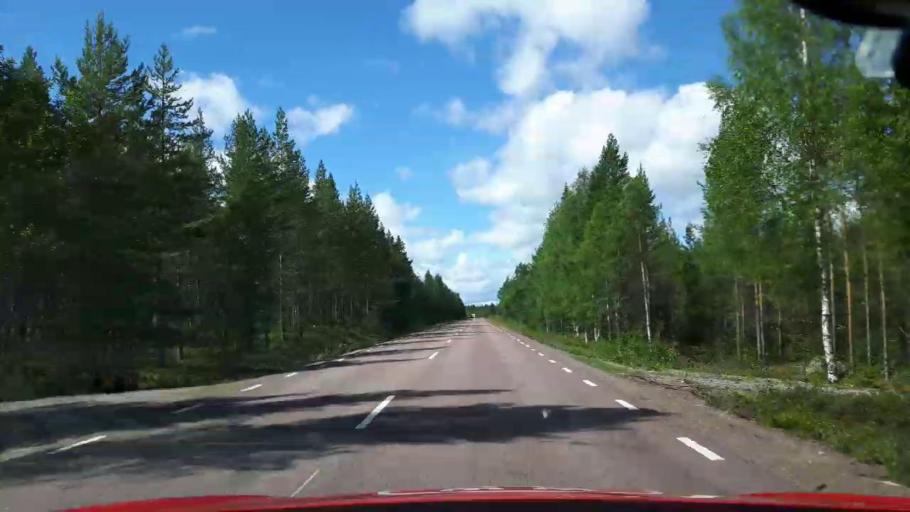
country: SE
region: Jaemtland
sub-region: Harjedalens Kommun
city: Sveg
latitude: 61.9963
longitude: 14.2434
